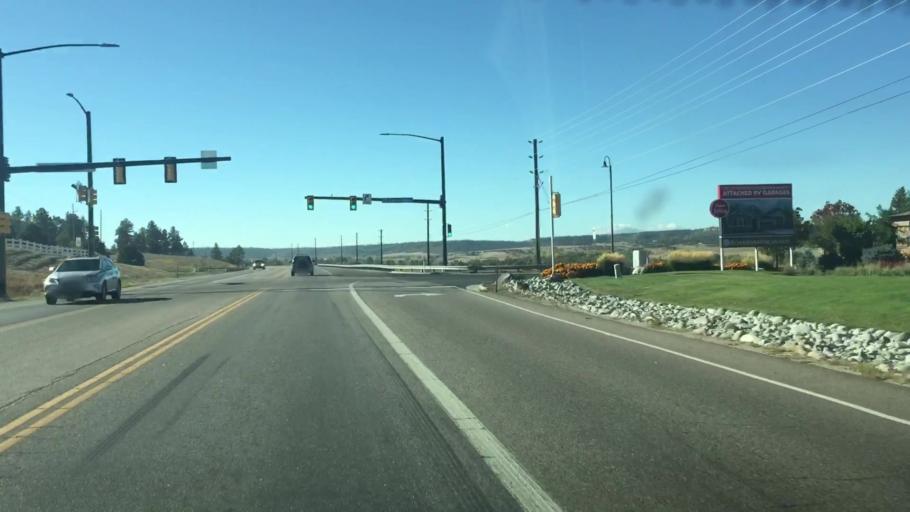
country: US
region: Colorado
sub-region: Douglas County
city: The Pinery
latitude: 39.4173
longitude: -104.7611
